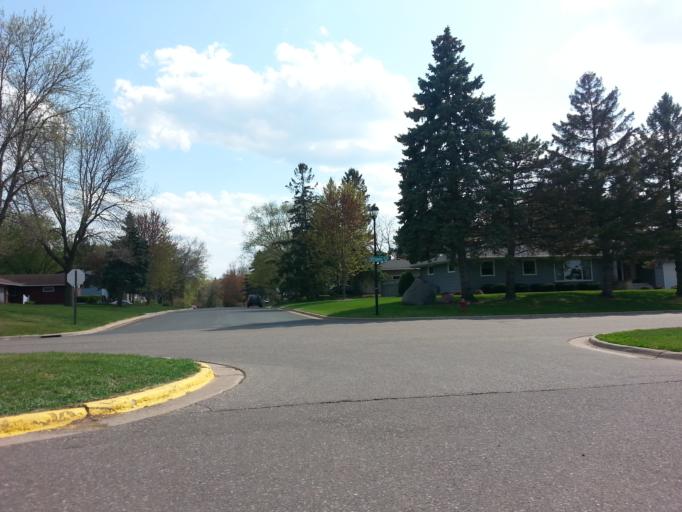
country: US
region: Minnesota
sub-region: Washington County
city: Stillwater
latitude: 45.0428
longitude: -92.8127
